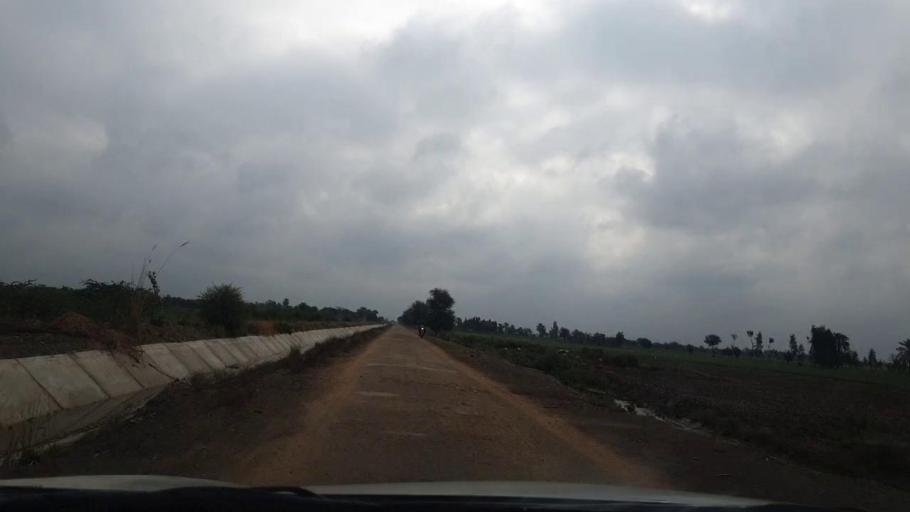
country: PK
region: Sindh
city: Tando Mittha Khan
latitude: 25.8821
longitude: 69.1388
